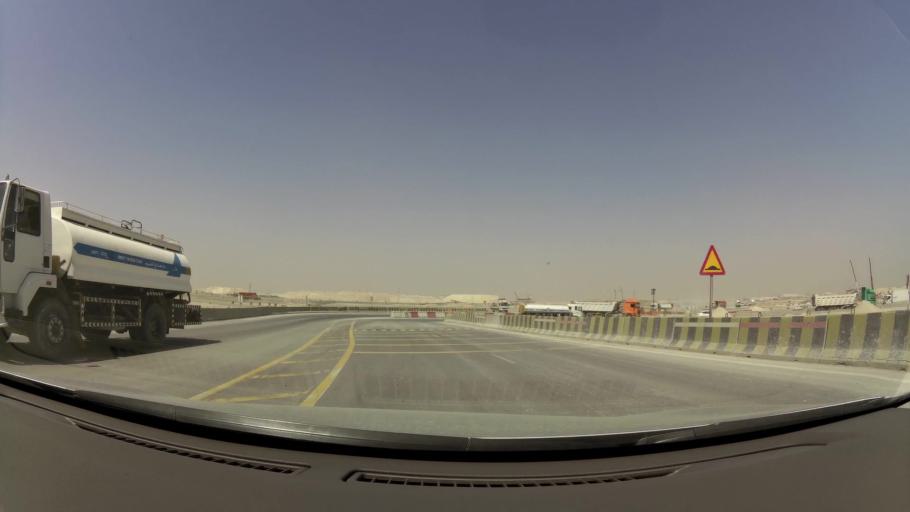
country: QA
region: Baladiyat Umm Salal
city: Umm Salal Muhammad
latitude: 25.4059
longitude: 51.4956
